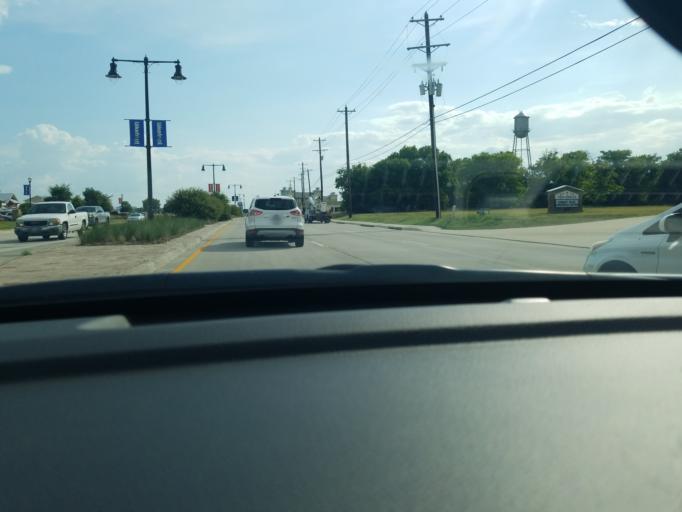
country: US
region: Texas
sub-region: Denton County
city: Little Elm
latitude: 33.1637
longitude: -96.9330
